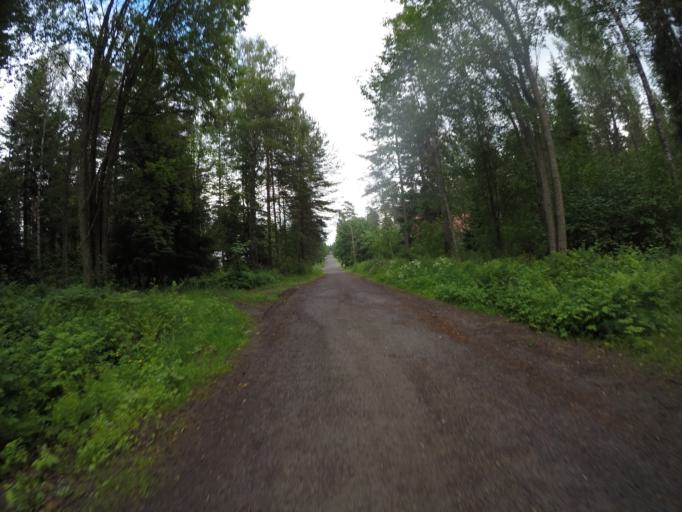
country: FI
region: Haeme
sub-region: Haemeenlinna
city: Haemeenlinna
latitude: 61.0136
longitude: 24.4869
